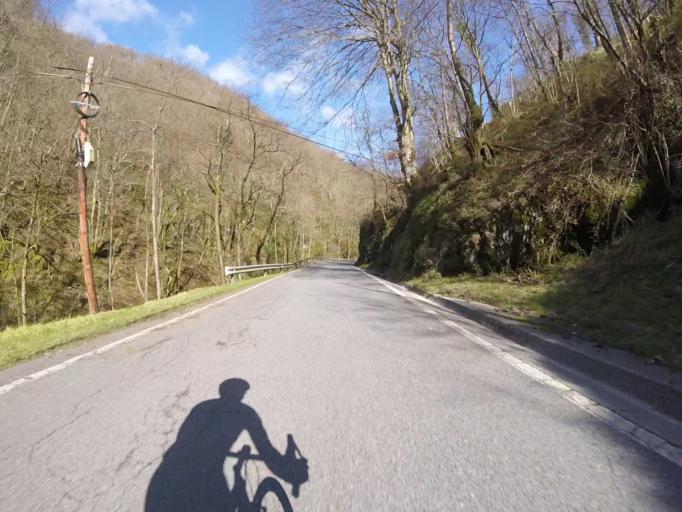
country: ES
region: Navarre
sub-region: Provincia de Navarra
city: Ezkurra
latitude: 43.1137
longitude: -1.8538
